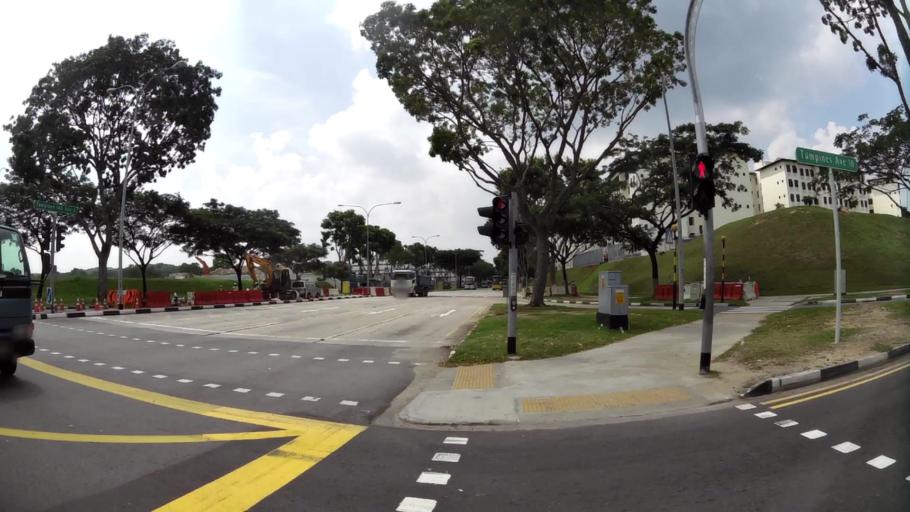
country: SG
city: Singapore
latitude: 1.3662
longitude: 103.9308
